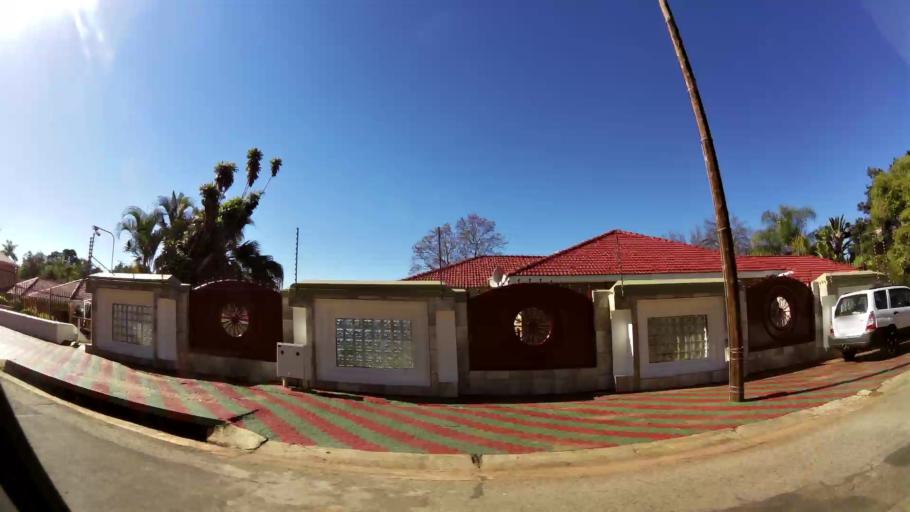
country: ZA
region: Limpopo
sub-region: Mopani District Municipality
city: Tzaneen
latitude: -23.8273
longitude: 30.1451
